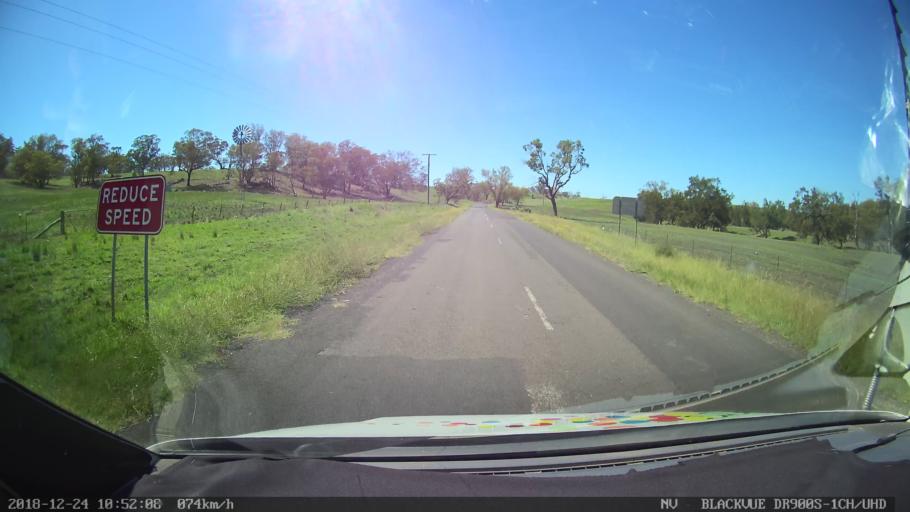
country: AU
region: New South Wales
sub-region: Upper Hunter Shire
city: Merriwa
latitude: -31.9773
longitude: 150.4211
